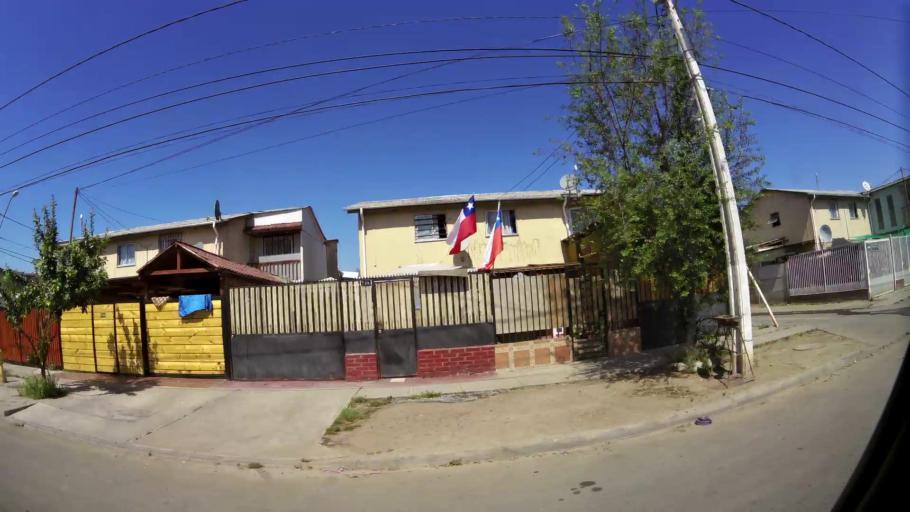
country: CL
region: Santiago Metropolitan
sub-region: Provincia de Santiago
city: Lo Prado
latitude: -33.4846
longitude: -70.7258
